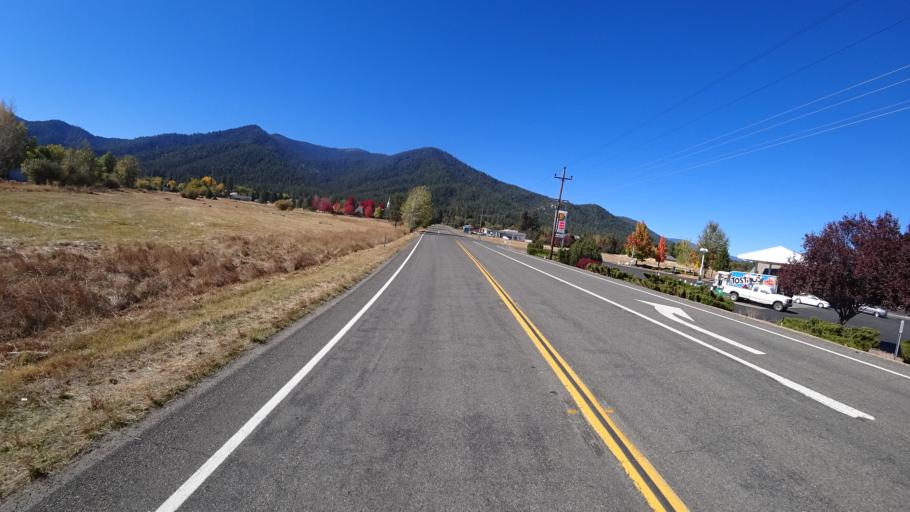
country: US
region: California
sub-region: Siskiyou County
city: Yreka
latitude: 41.4619
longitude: -122.8897
